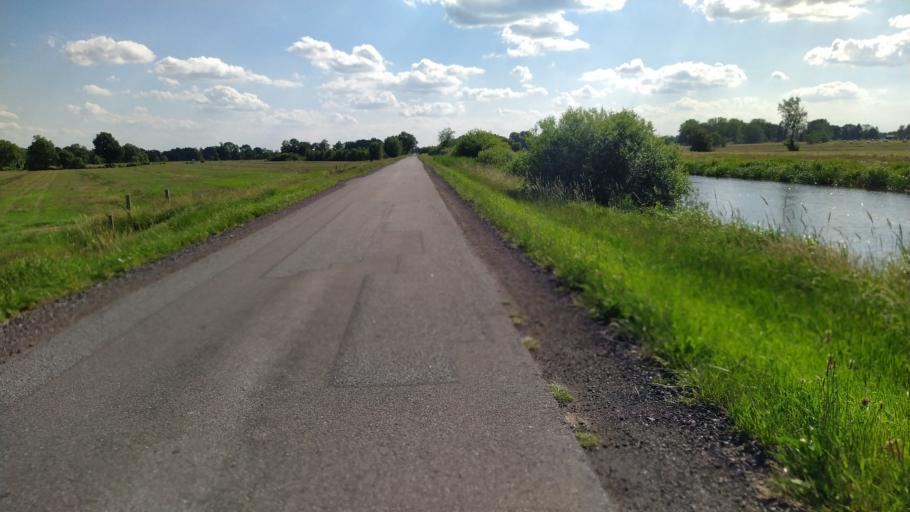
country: DE
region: Lower Saxony
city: Odisheim
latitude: 53.6664
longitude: 8.9094
